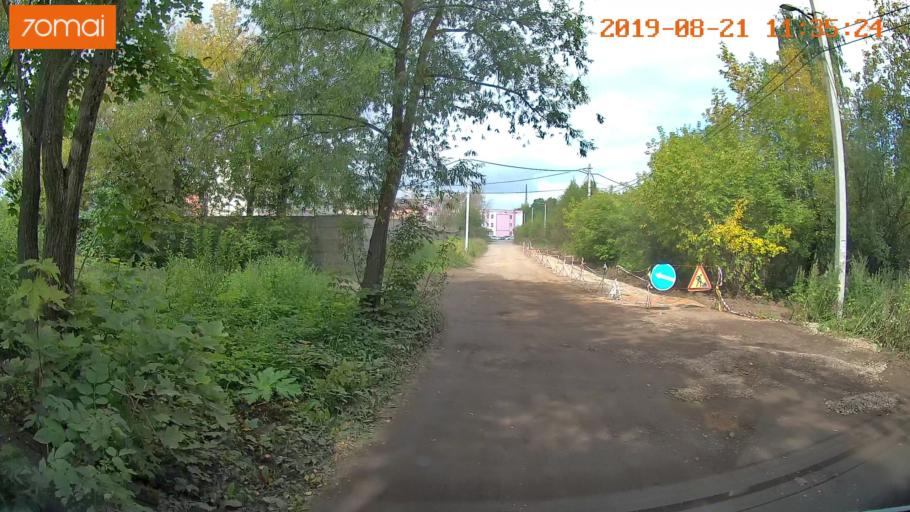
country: RU
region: Ivanovo
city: Novo-Talitsy
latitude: 56.9898
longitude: 40.9104
